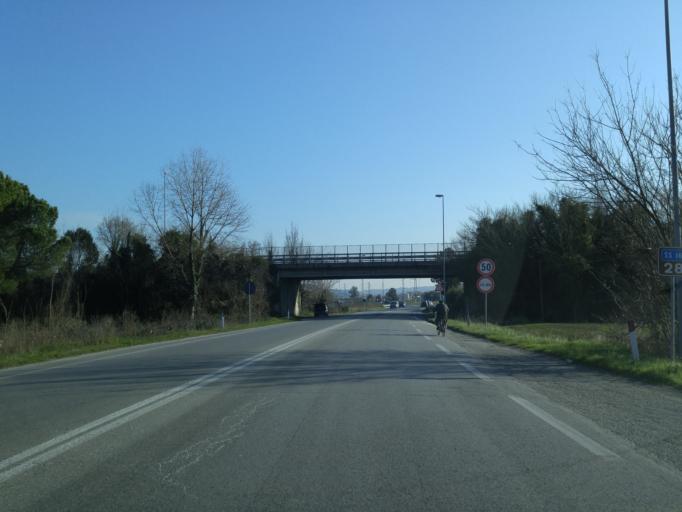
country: IT
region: Emilia-Romagna
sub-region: Provincia di Rimini
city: Cattolica
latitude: 43.9564
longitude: 12.7271
